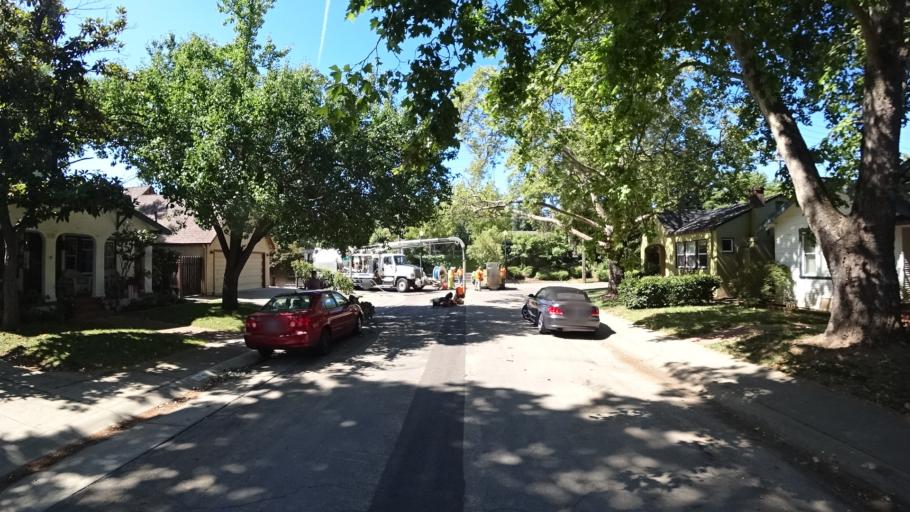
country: US
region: California
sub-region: Sacramento County
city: Sacramento
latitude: 38.5610
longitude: -121.4567
